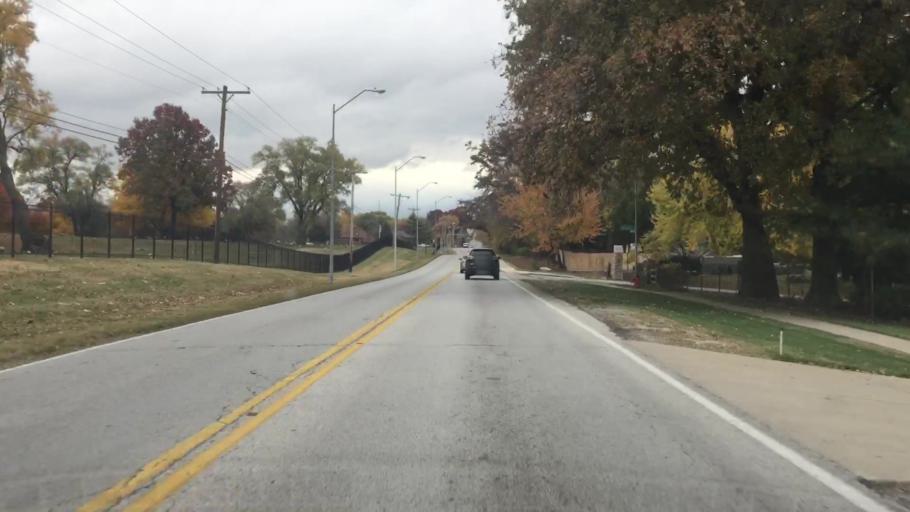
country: US
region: Missouri
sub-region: Jackson County
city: Raytown
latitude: 38.9953
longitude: -94.4871
